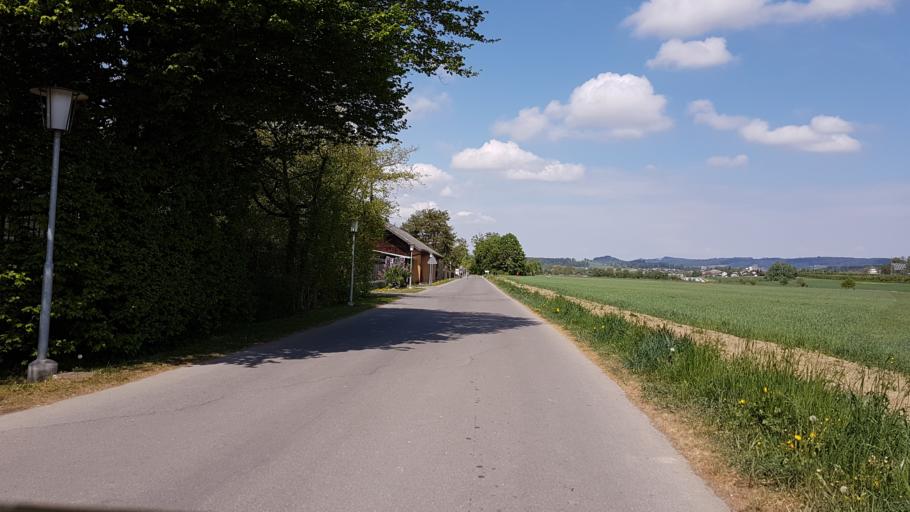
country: CH
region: Bern
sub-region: Bern-Mittelland District
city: Munsingen
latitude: 46.8809
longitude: 7.5557
